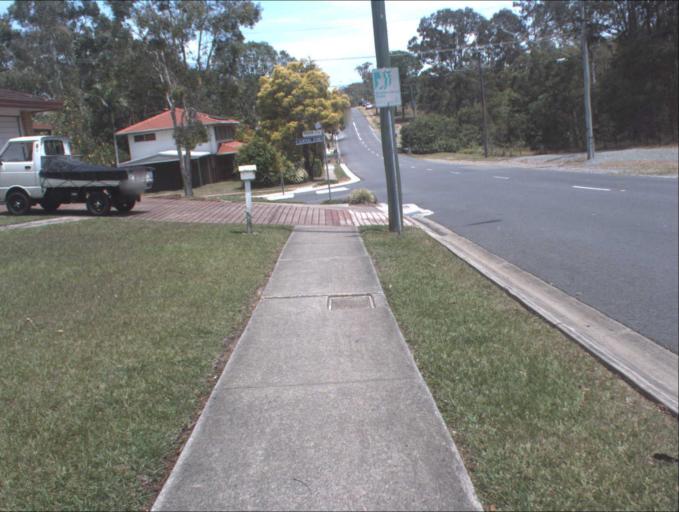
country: AU
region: Queensland
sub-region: Logan
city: Rochedale South
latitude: -27.5891
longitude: 153.1358
